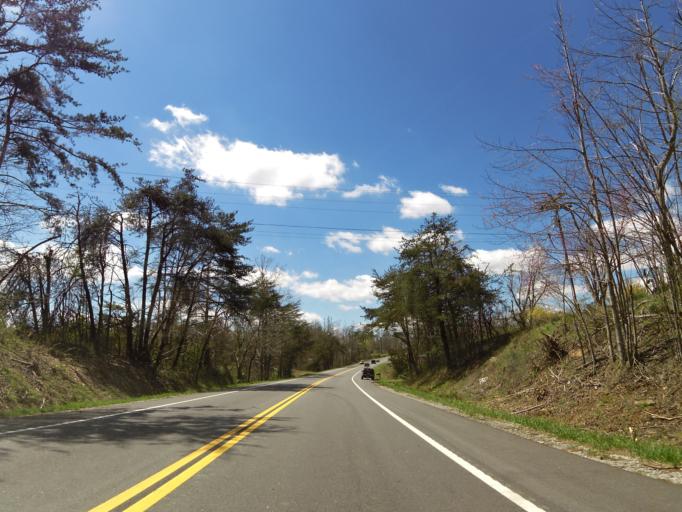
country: US
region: Tennessee
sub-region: Putnam County
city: Monterey
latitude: 35.9656
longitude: -85.2354
